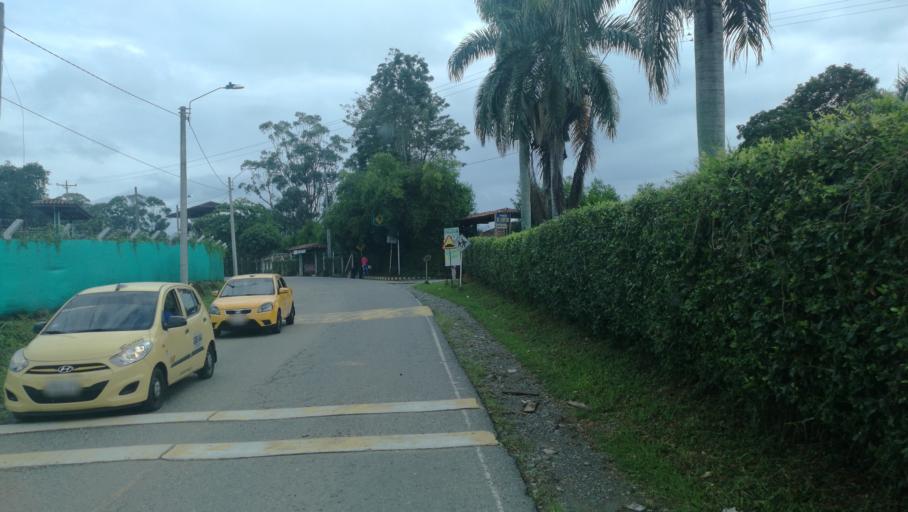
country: CO
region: Quindio
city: Montenegro
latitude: 4.5397
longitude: -75.7729
